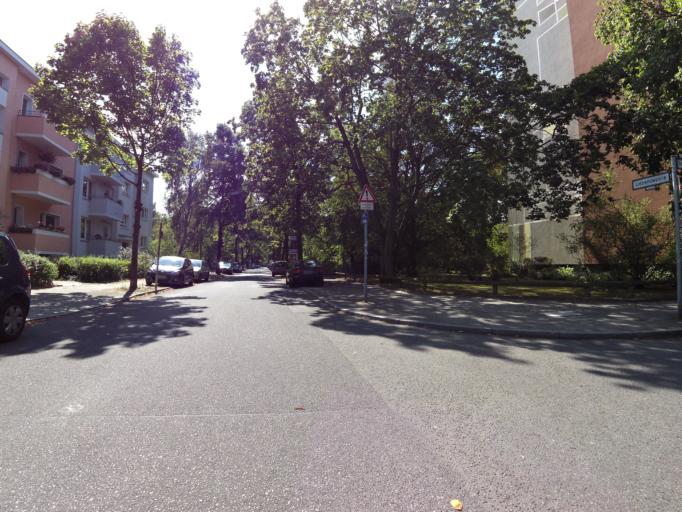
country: DE
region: Berlin
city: Lankwitz
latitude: 52.4492
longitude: 13.3496
